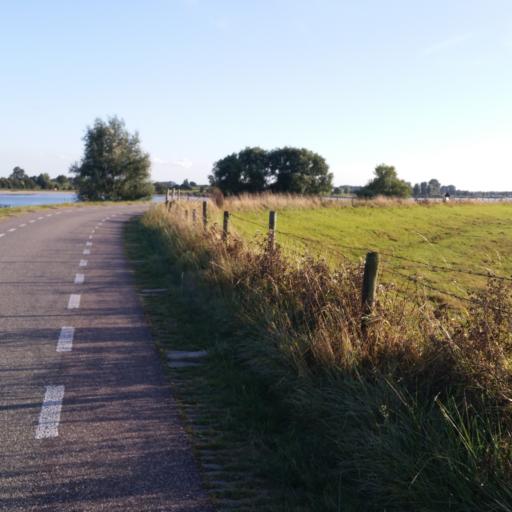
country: NL
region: Utrecht
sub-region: Gemeente Lopik
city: Lopik
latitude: 51.9748
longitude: 4.9843
